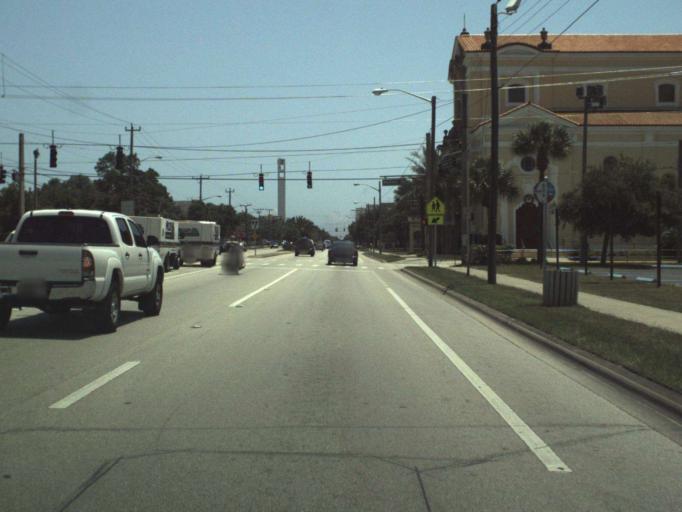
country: US
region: Florida
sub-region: Volusia County
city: Daytona Beach
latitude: 29.2185
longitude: -81.0270
